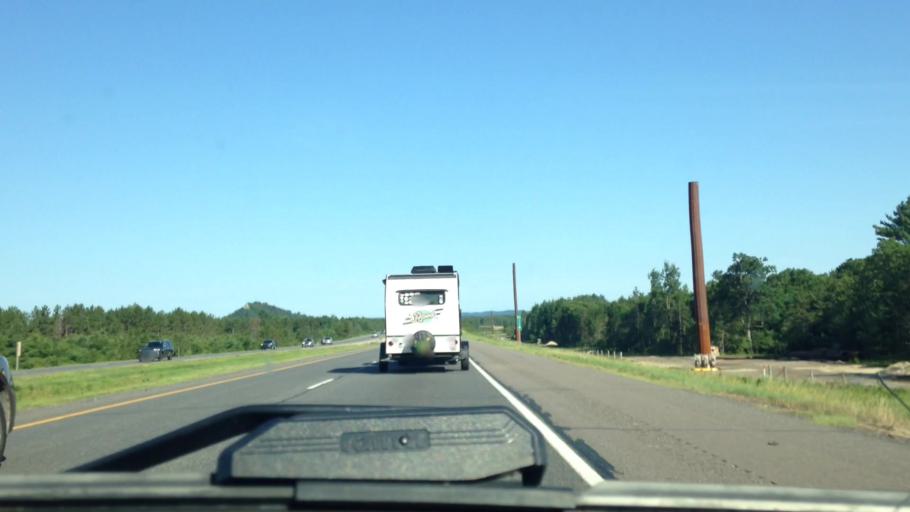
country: US
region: Wisconsin
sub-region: Jackson County
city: Black River Falls
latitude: 44.2720
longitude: -90.7896
